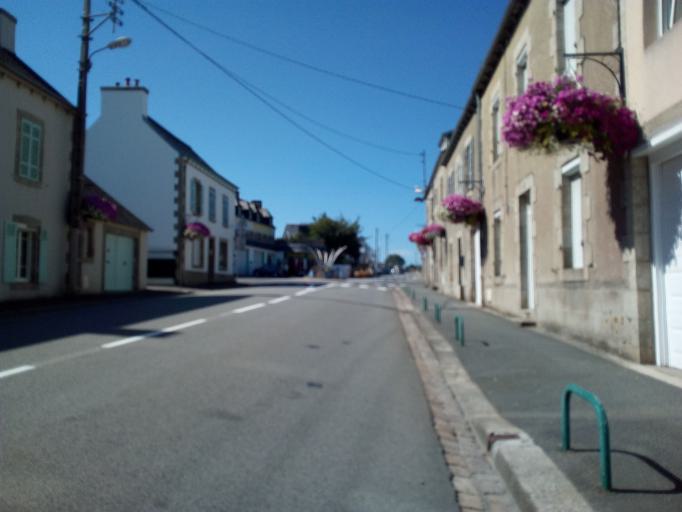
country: FR
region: Brittany
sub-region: Departement du Finistere
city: Landivisiau
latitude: 48.5123
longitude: -4.0707
